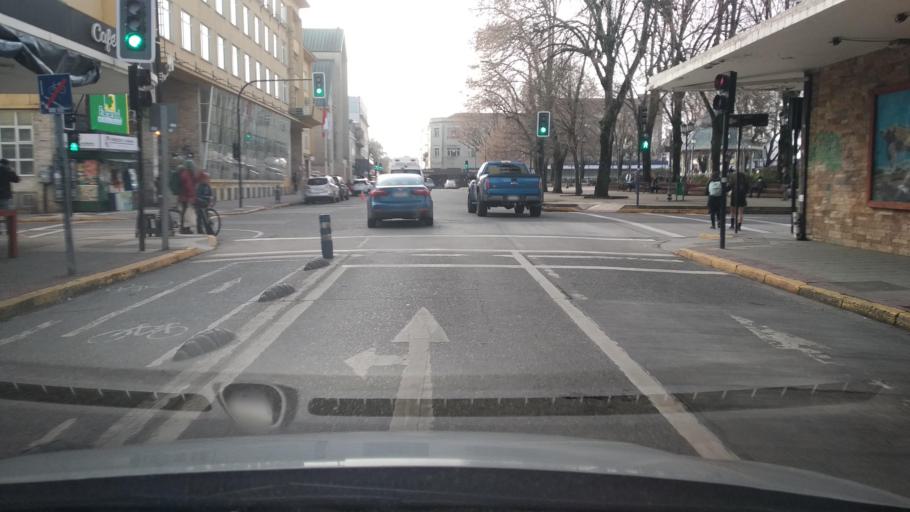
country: CL
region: Los Rios
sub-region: Provincia de Valdivia
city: Valdivia
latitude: -39.8150
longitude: -73.2464
